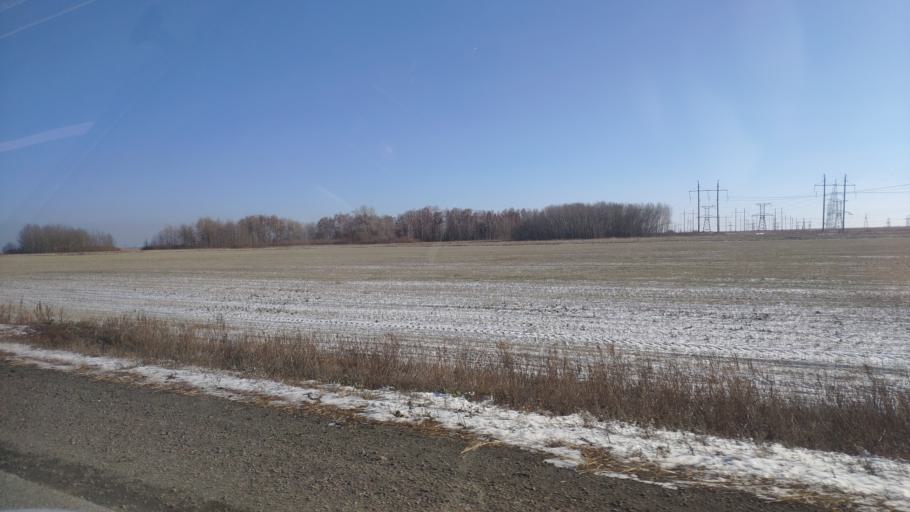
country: RU
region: Orenburg
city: Mednogorsk
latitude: 51.3232
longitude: 57.6046
